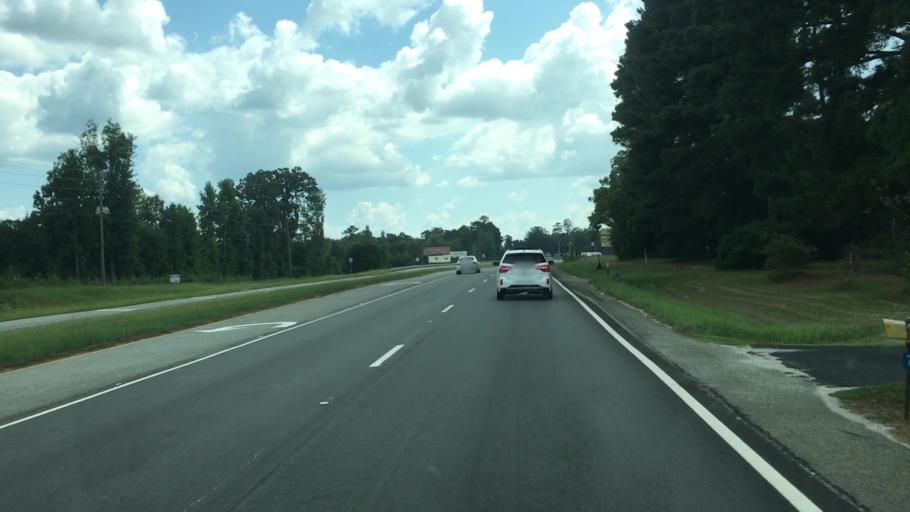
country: US
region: Georgia
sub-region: Putnam County
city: Eatonton
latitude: 33.3513
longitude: -83.3912
